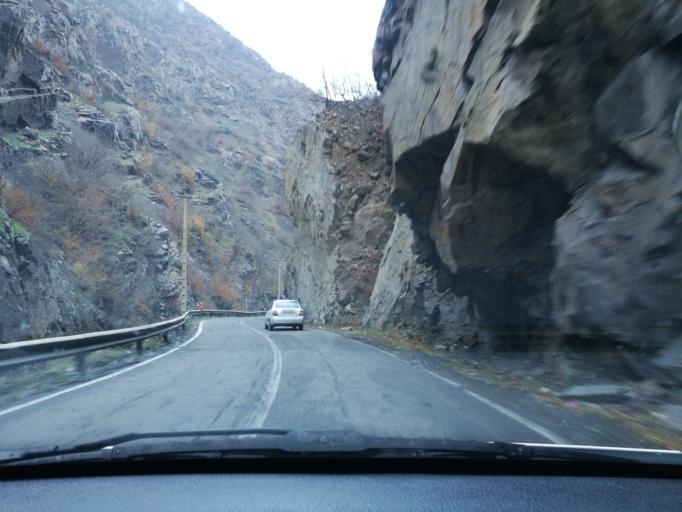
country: IR
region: Mazandaran
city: Chalus
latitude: 36.2818
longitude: 51.2430
